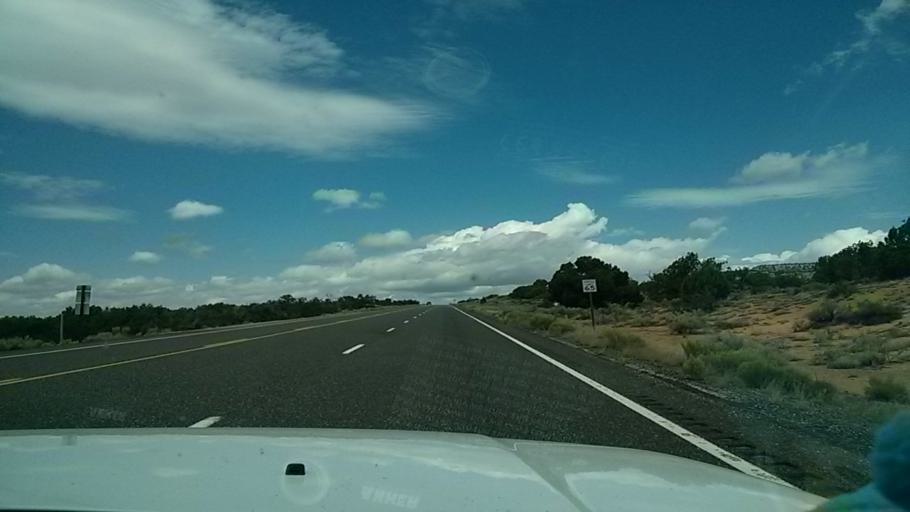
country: US
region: Utah
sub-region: Kane County
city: Kanab
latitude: 37.1638
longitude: -112.5955
